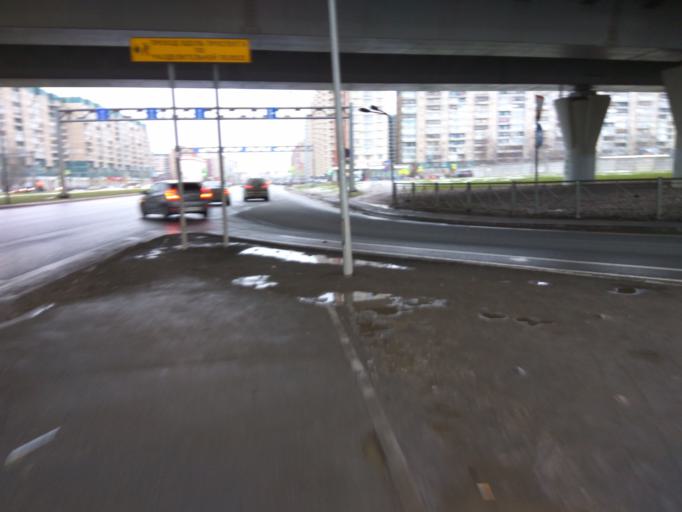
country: RU
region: St.-Petersburg
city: Staraya Derevnya
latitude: 60.0038
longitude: 30.2325
